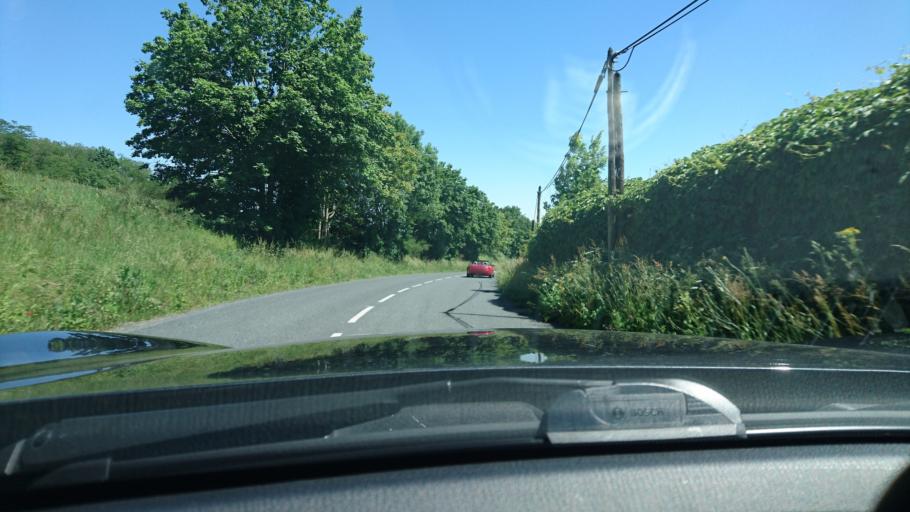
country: FR
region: Rhone-Alpes
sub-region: Departement du Rhone
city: Vaugneray
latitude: 45.7271
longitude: 4.6479
